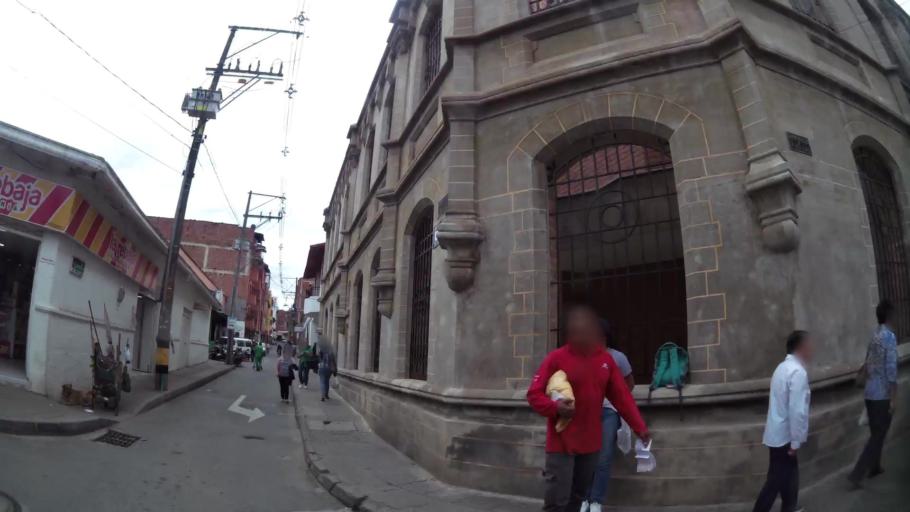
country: CO
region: Antioquia
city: Rionegro
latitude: 6.1525
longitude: -75.3738
